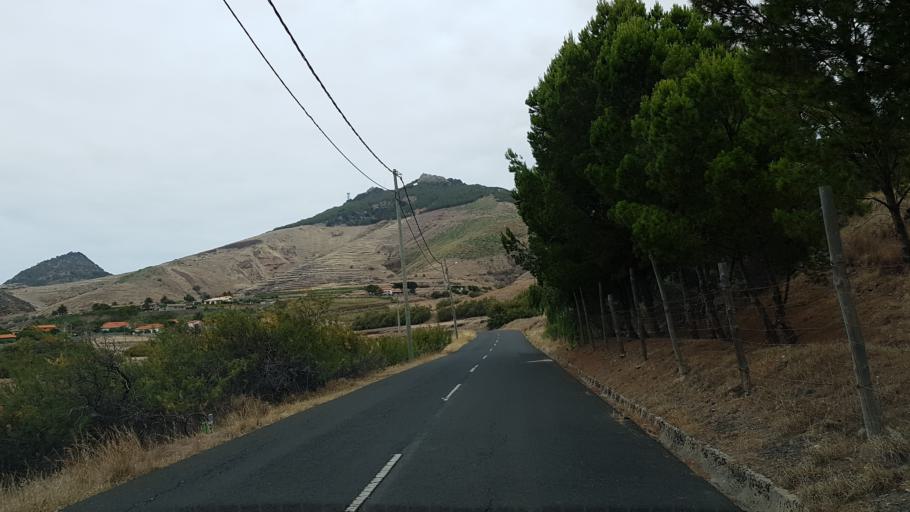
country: PT
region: Madeira
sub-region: Porto Santo
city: Vila de Porto Santo
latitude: 33.0726
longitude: -16.3083
